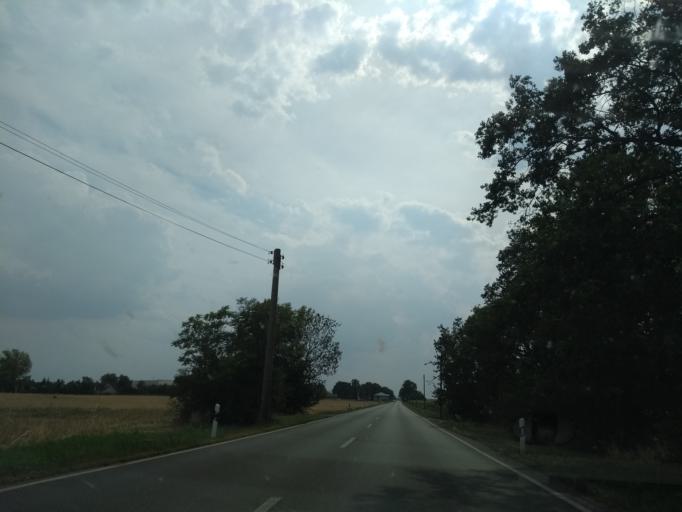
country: DE
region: Thuringia
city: Hirschfeld
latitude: 50.9637
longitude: 12.1316
